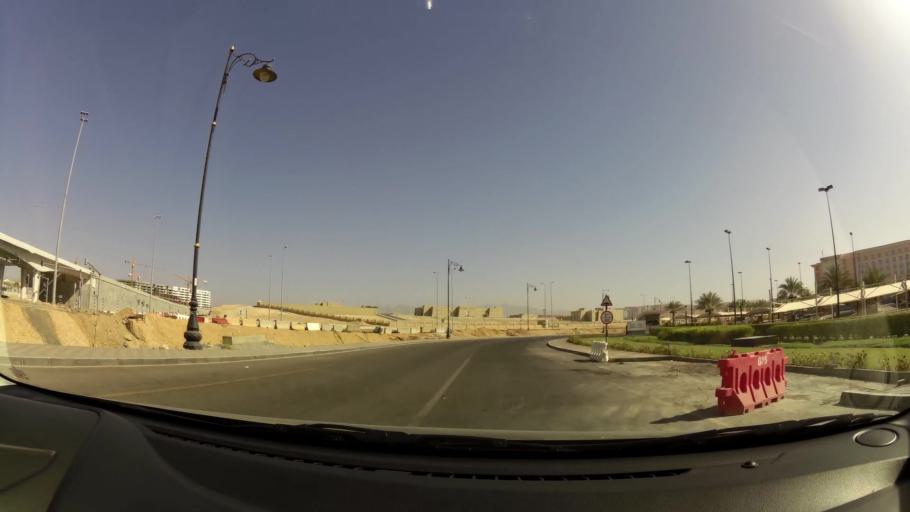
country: OM
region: Muhafazat Masqat
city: Bawshar
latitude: 23.5784
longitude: 58.2941
